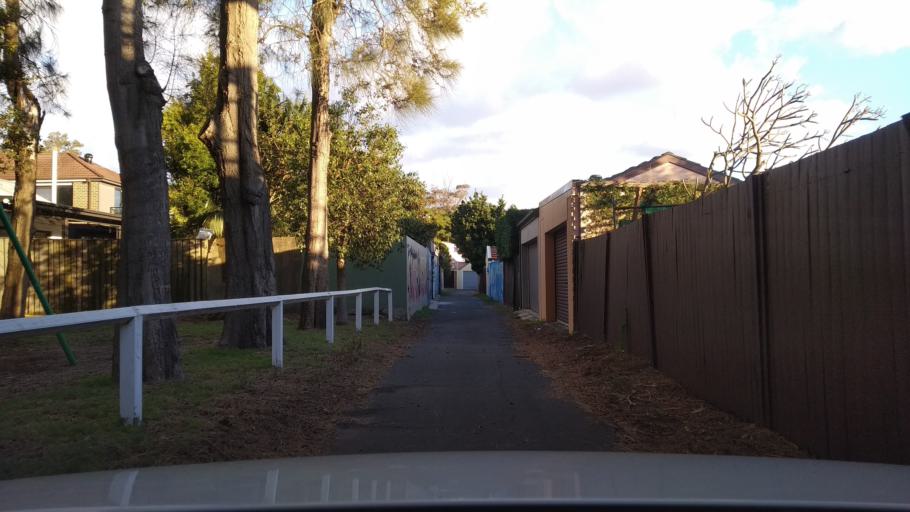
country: AU
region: New South Wales
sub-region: Waverley
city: North Bondi
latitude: -33.8827
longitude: 151.2719
